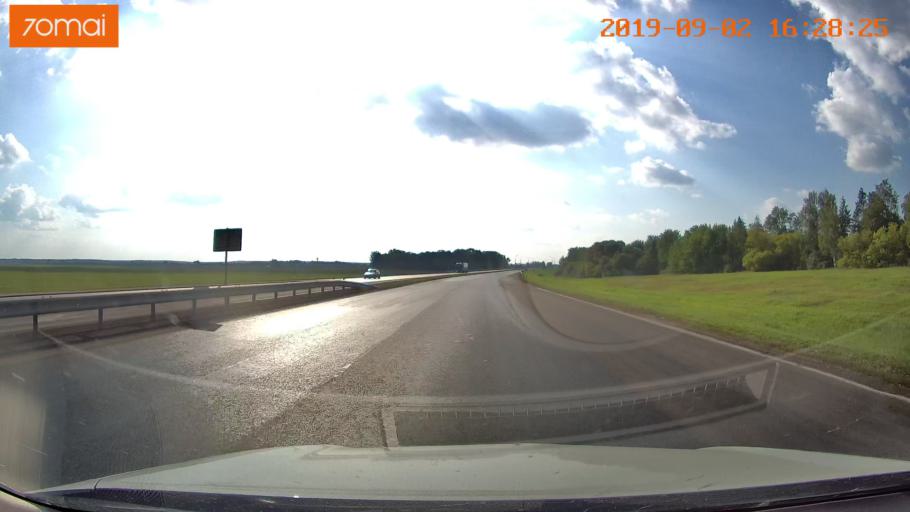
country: BY
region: Minsk
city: Smilavichy
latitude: 53.7637
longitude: 28.1776
